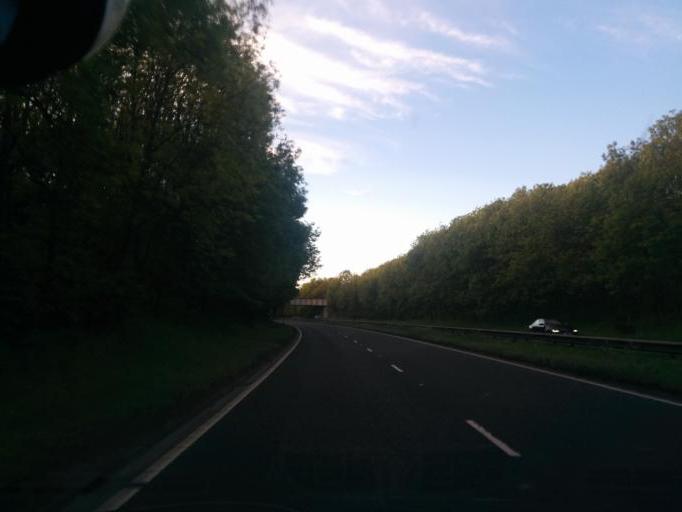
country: GB
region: England
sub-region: Northumberland
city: Bedlington
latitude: 55.1201
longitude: -1.5547
